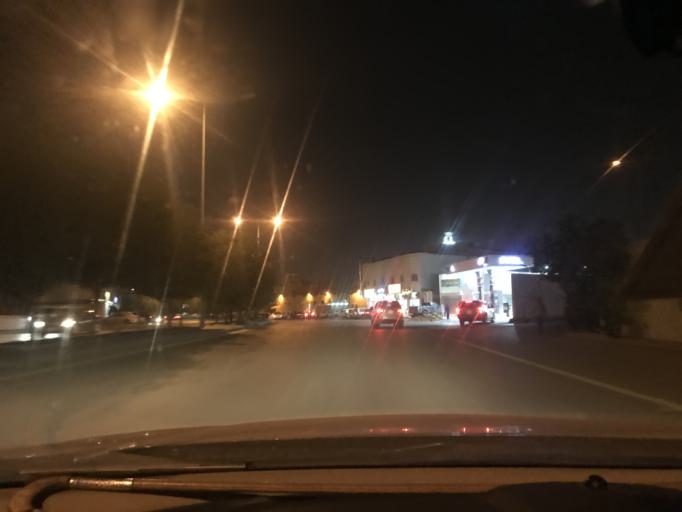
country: SA
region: Ar Riyad
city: Riyadh
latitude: 24.7464
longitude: 46.7533
